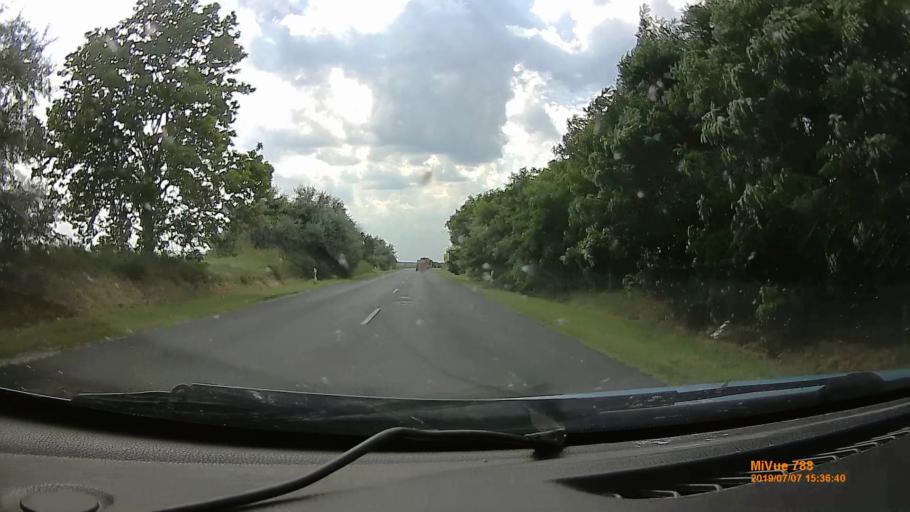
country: HU
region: Jasz-Nagykun-Szolnok
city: Jaszbereny
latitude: 47.4820
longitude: 19.9585
